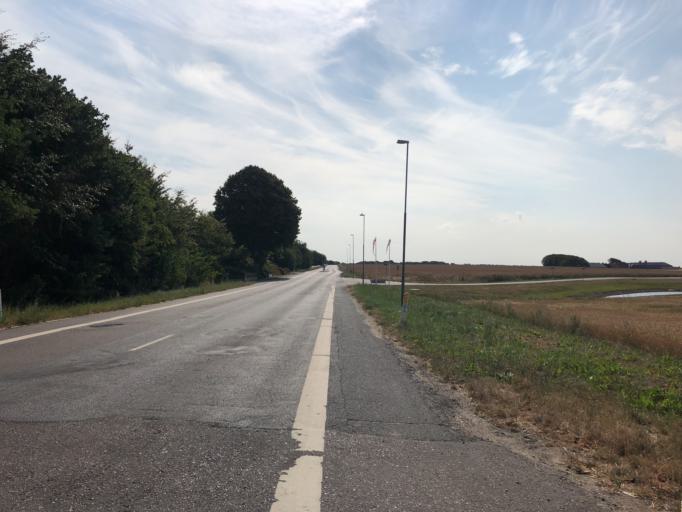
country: DK
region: Central Jutland
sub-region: Holstebro Kommune
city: Vinderup
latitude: 56.5902
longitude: 8.7879
